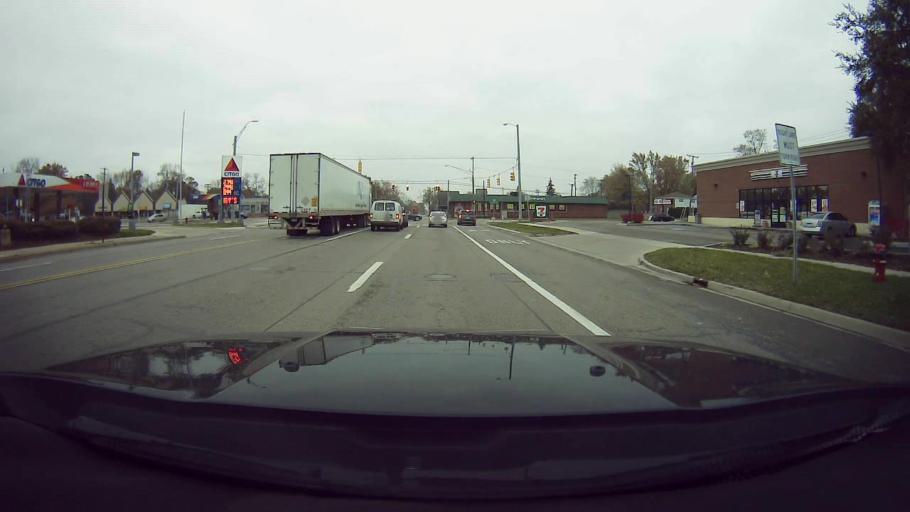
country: US
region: Michigan
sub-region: Oakland County
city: Clawson
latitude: 42.5341
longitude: -83.1358
